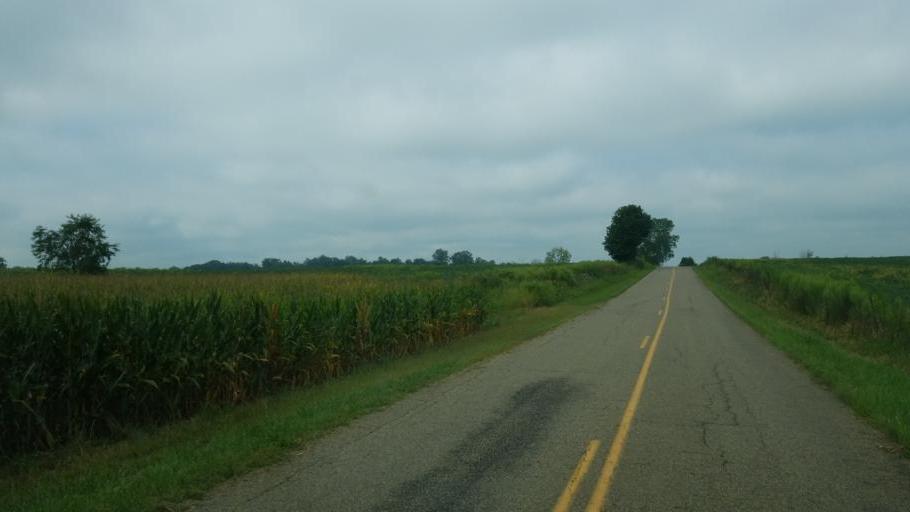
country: US
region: Ohio
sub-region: Licking County
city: Utica
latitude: 40.2763
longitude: -82.4414
